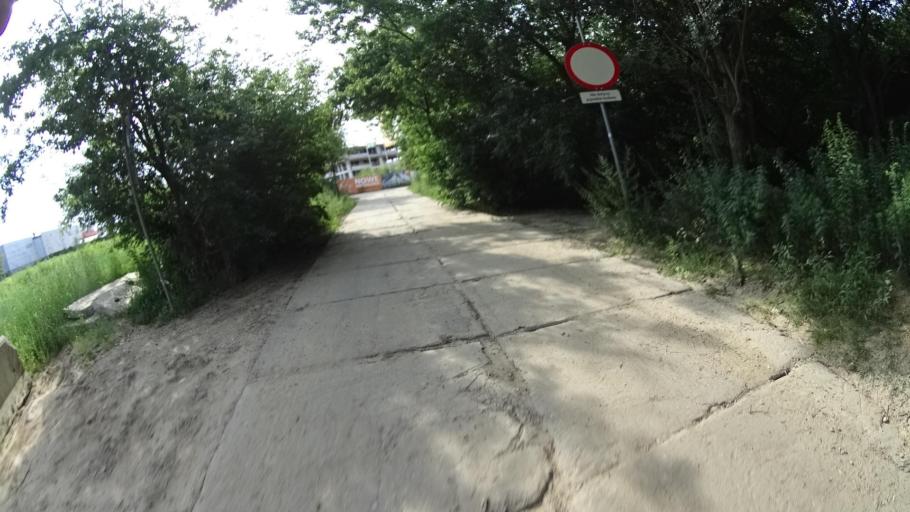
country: PL
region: Masovian Voivodeship
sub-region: Warszawa
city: Ursus
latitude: 52.2184
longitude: 20.8918
